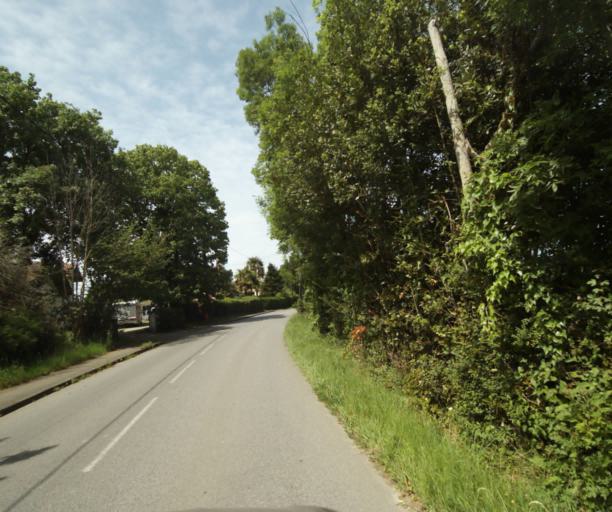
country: FR
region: Aquitaine
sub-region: Departement des Pyrenees-Atlantiques
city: Mouguerre
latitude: 43.4583
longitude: -1.4376
